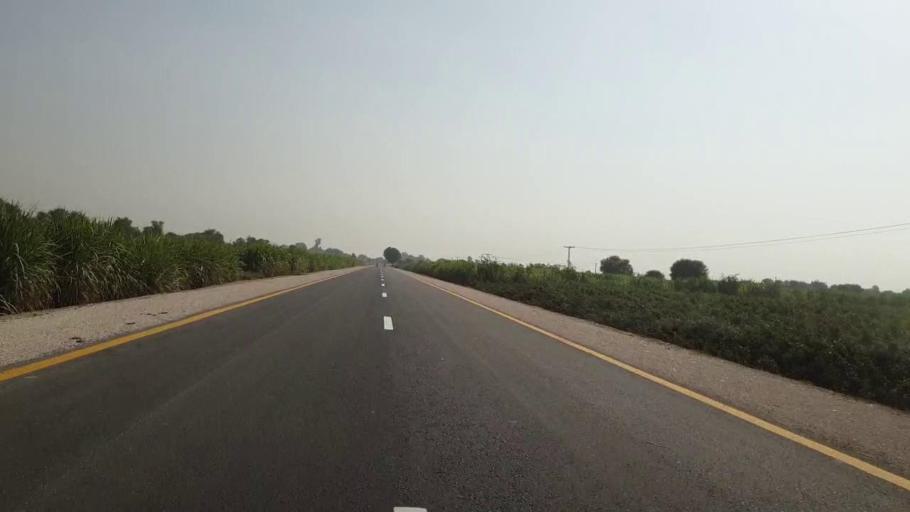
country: PK
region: Sindh
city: Bhan
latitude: 26.6086
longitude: 67.7789
